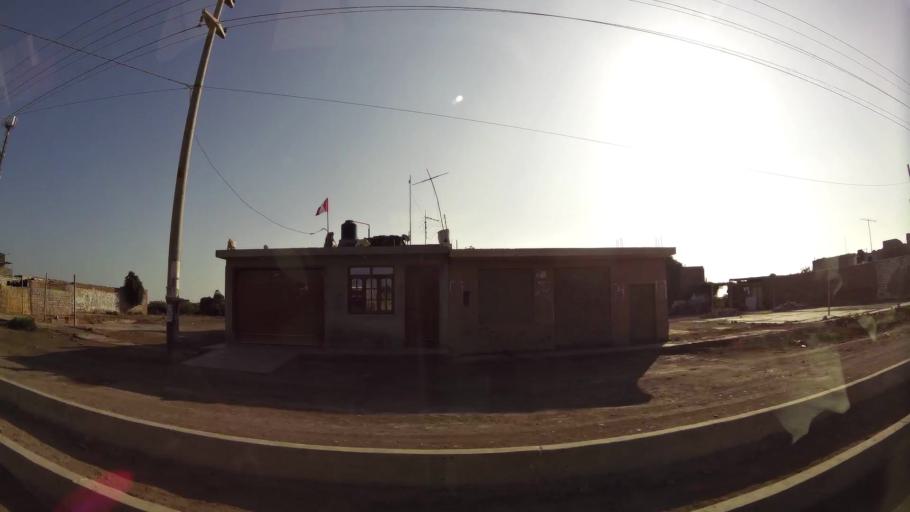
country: PE
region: Ica
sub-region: Provincia de Chincha
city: Chincha Baja
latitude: -13.4563
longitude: -76.1822
